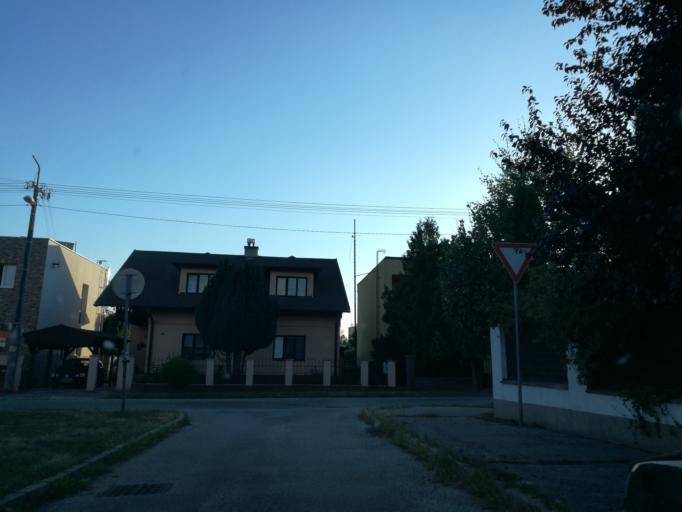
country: SK
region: Nitriansky
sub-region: Okres Nitra
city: Nitra
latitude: 48.3094
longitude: 18.1179
